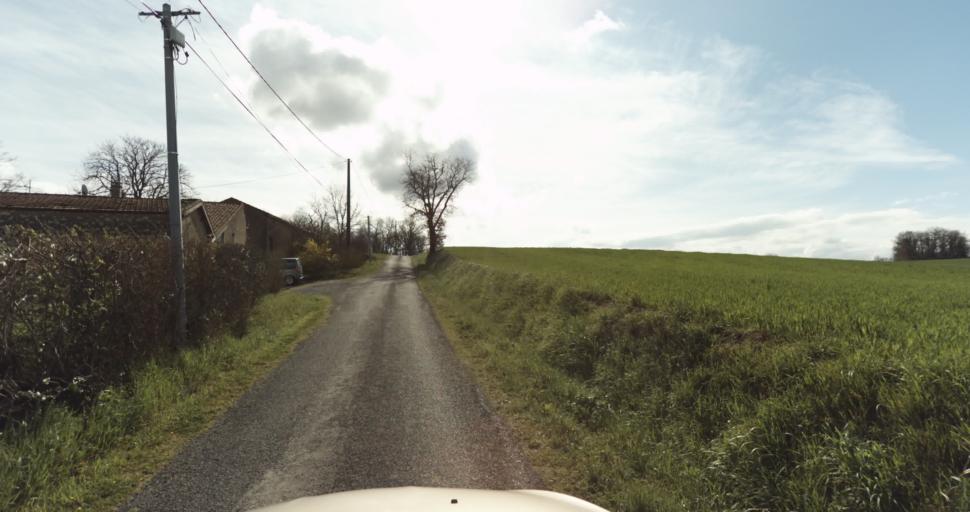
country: FR
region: Midi-Pyrenees
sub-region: Departement du Tarn
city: Puygouzon
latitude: 43.8662
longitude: 2.1750
